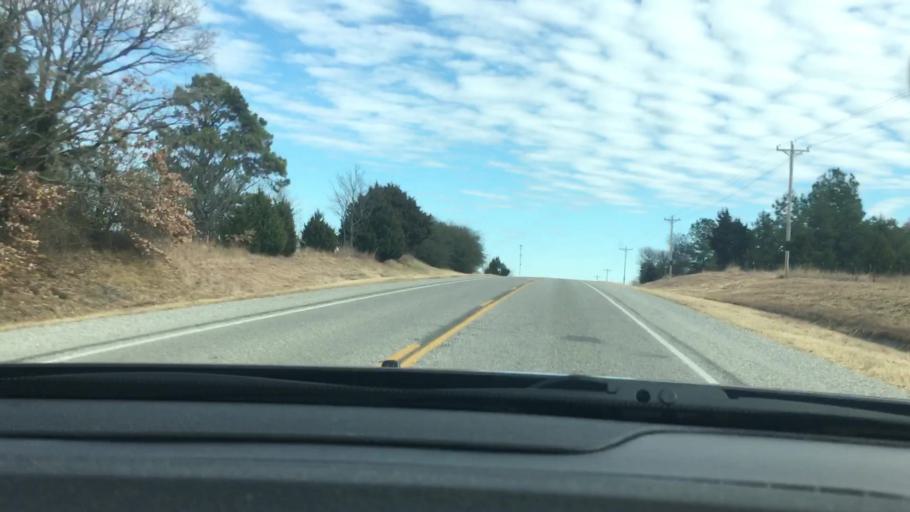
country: US
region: Oklahoma
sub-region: Garvin County
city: Stratford
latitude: 34.7966
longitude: -97.0620
